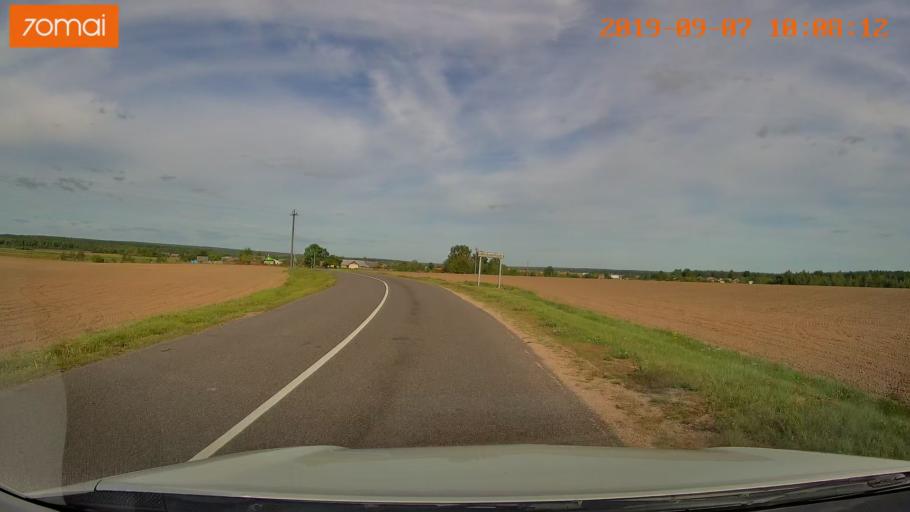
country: BY
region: Grodnenskaya
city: Voranava
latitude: 54.0847
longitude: 25.3910
